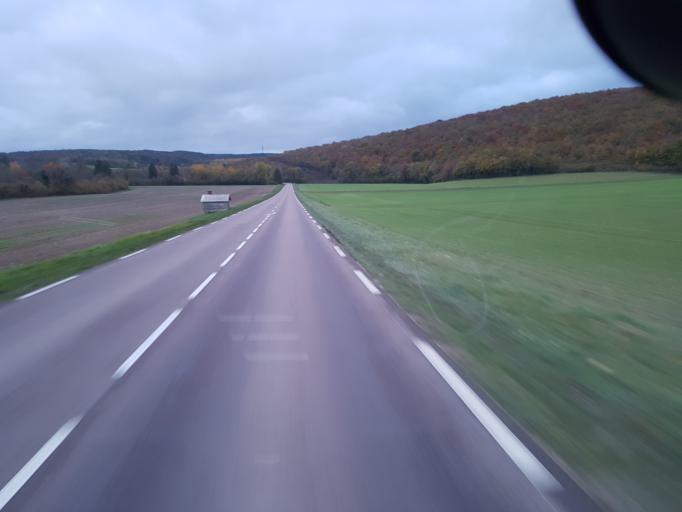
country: FR
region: Champagne-Ardenne
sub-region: Departement de l'Aube
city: Mussy-sur-Seine
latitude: 48.0045
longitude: 4.4743
